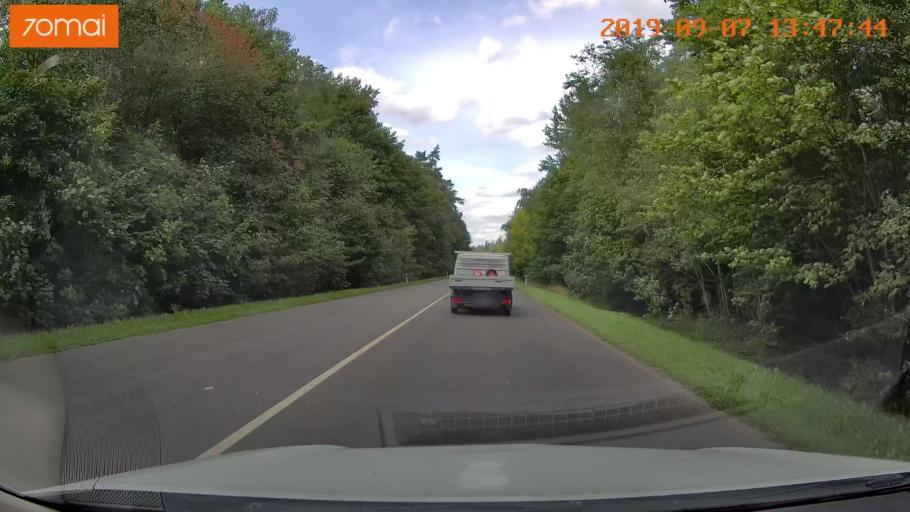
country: LT
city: Baltoji Voke
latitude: 54.5989
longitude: 25.2103
